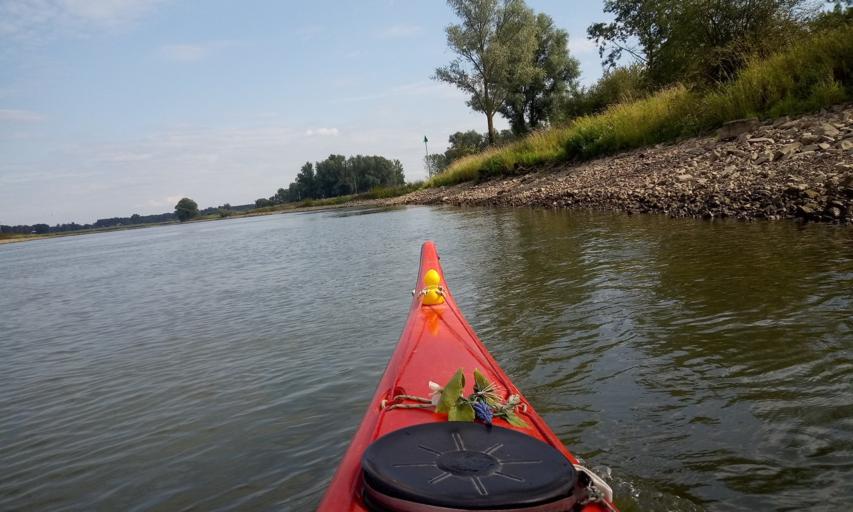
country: NL
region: Gelderland
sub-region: Gemeente Lochem
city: Gorssel
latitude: 52.1817
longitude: 6.1795
